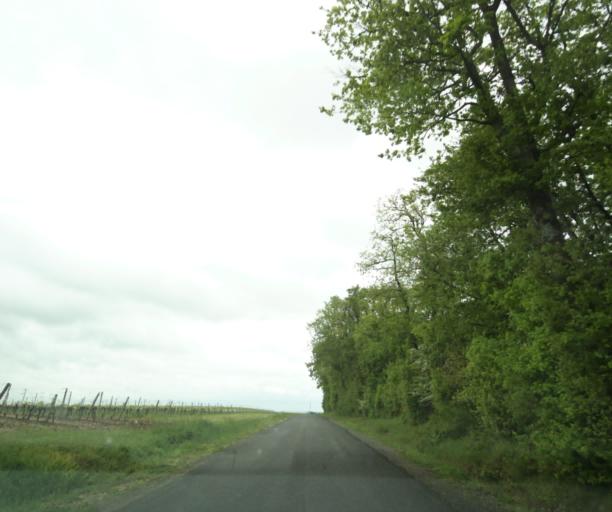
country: FR
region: Poitou-Charentes
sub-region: Departement de la Charente-Maritime
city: Perignac
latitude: 45.6736
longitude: -0.4959
